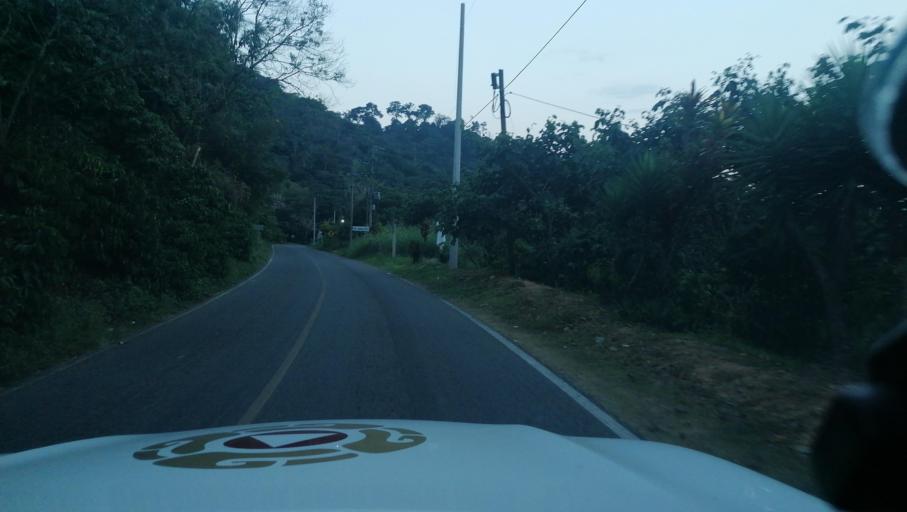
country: MX
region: Chiapas
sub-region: Cacahoatan
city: Benito Juarez
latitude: 15.0507
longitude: -92.2438
